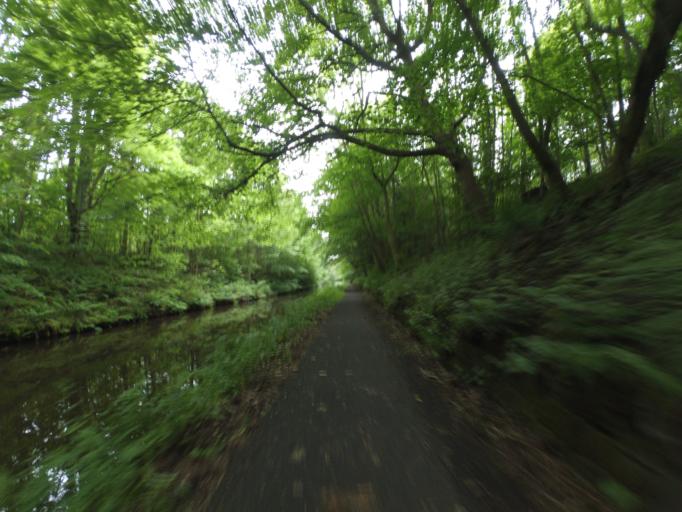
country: GB
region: Scotland
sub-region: West Lothian
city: Broxburn
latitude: 55.9707
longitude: -3.4853
